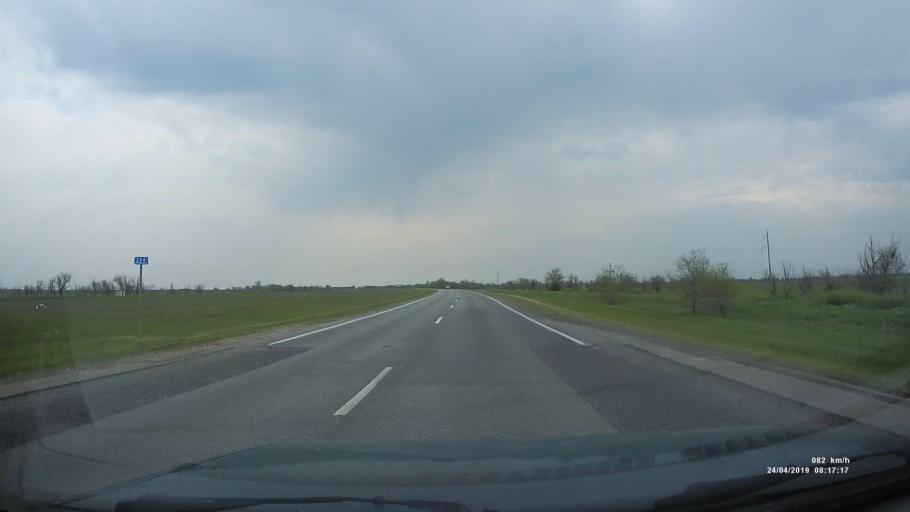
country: RU
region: Kalmykiya
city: Priyutnoye
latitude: 46.0980
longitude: 43.6272
